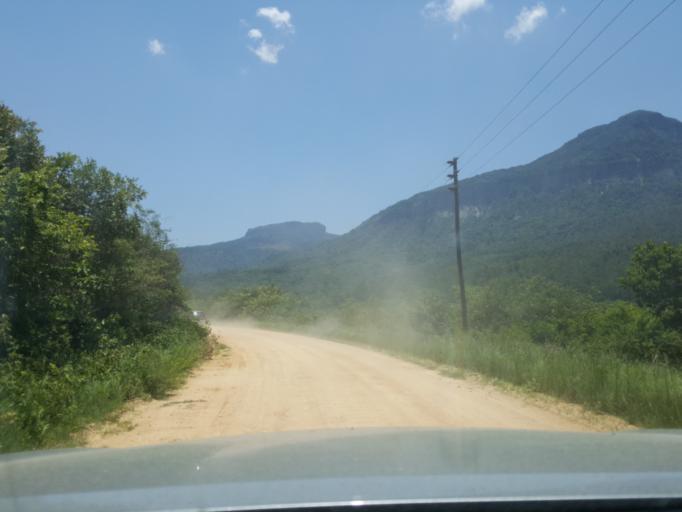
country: ZA
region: Limpopo
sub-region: Mopani District Municipality
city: Hoedspruit
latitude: -24.5968
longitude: 30.9197
